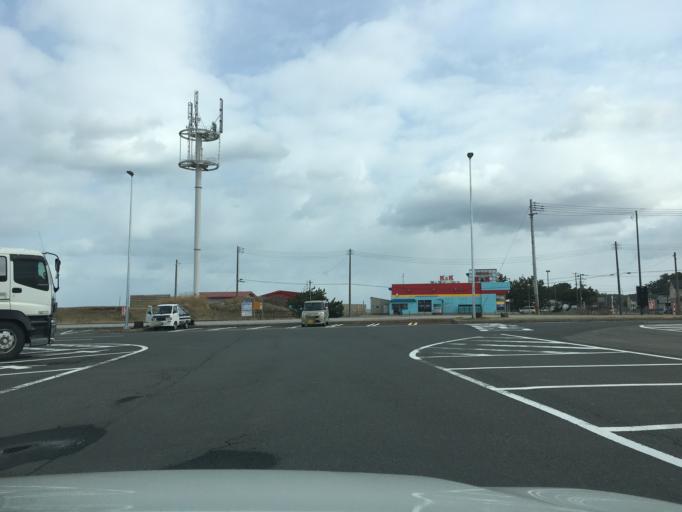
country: JP
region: Yamagata
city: Yuza
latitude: 39.2207
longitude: 139.9011
